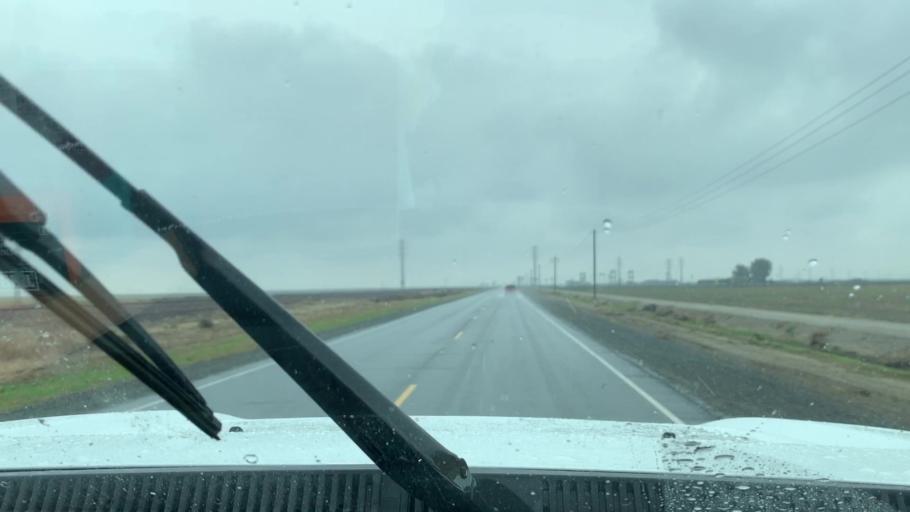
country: US
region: California
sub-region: Tulare County
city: Alpaugh
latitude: 35.9571
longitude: -119.4533
